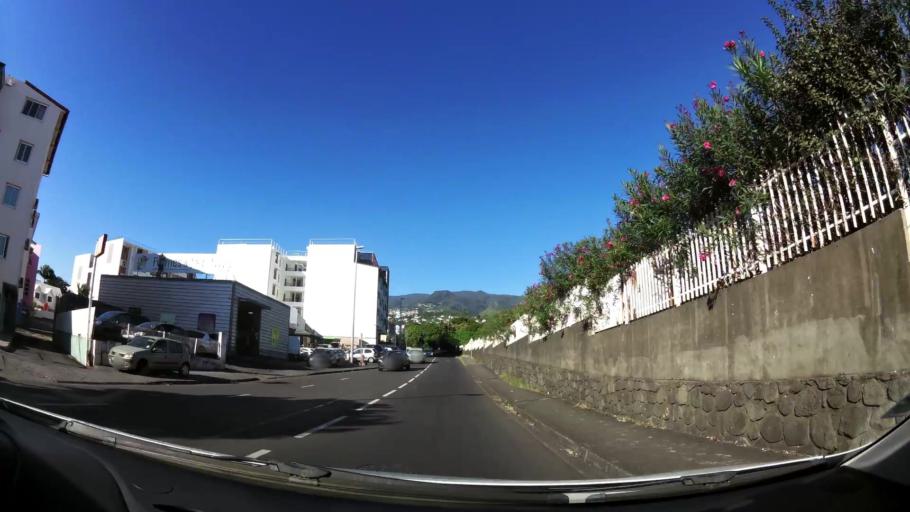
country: RE
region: Reunion
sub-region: Reunion
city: Saint-Denis
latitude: -20.8980
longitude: 55.4753
